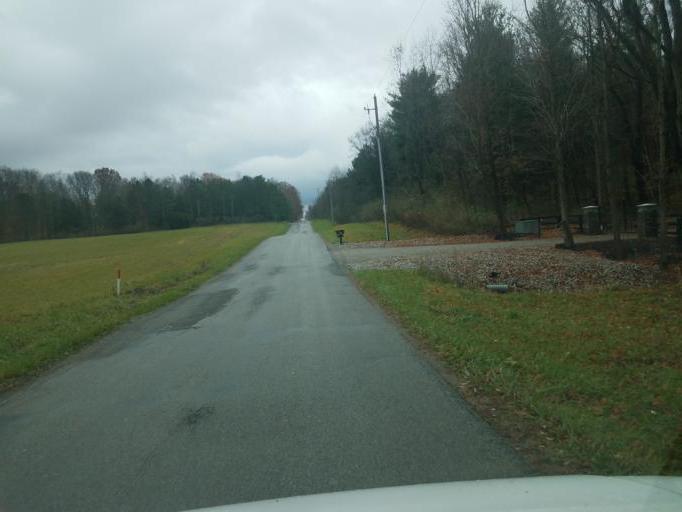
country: US
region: Ohio
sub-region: Morrow County
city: Mount Gilead
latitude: 40.6008
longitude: -82.8047
